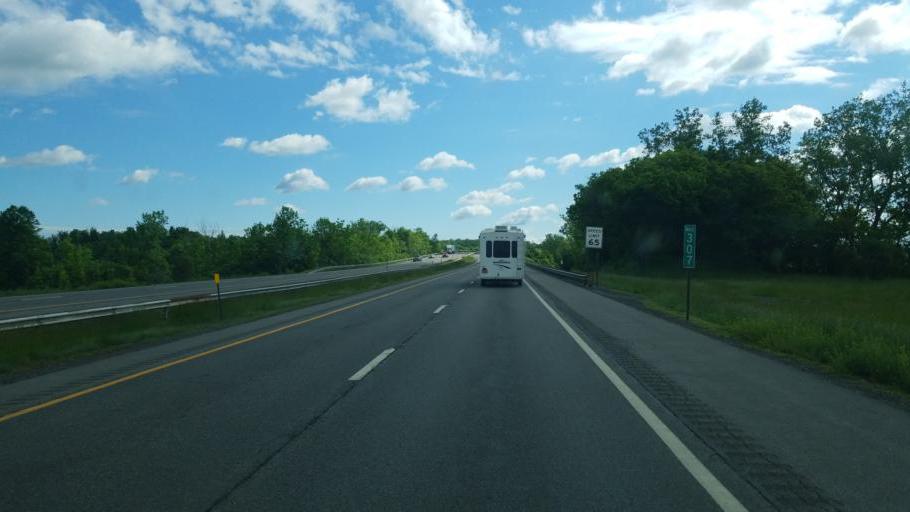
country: US
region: New York
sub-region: Cayuga County
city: Port Byron
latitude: 43.0476
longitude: -76.6165
